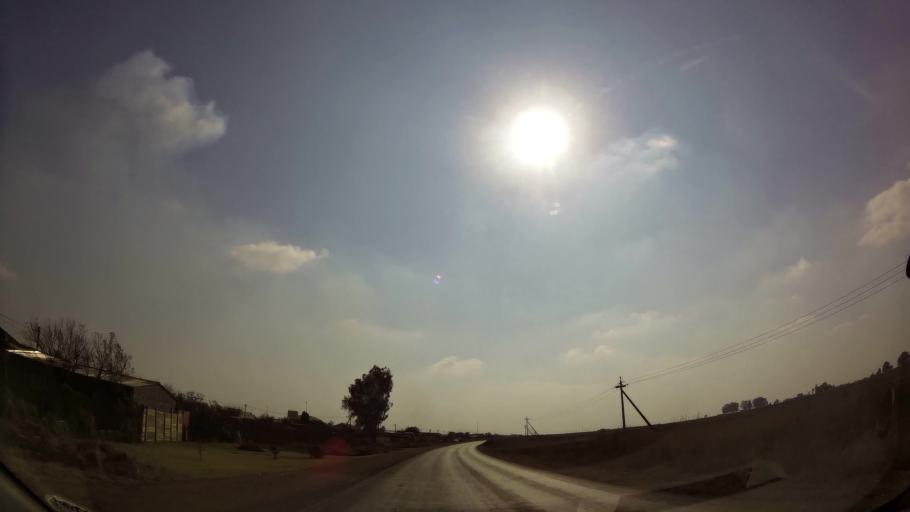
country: ZA
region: Gauteng
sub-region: Ekurhuleni Metropolitan Municipality
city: Springs
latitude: -26.1153
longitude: 28.4879
